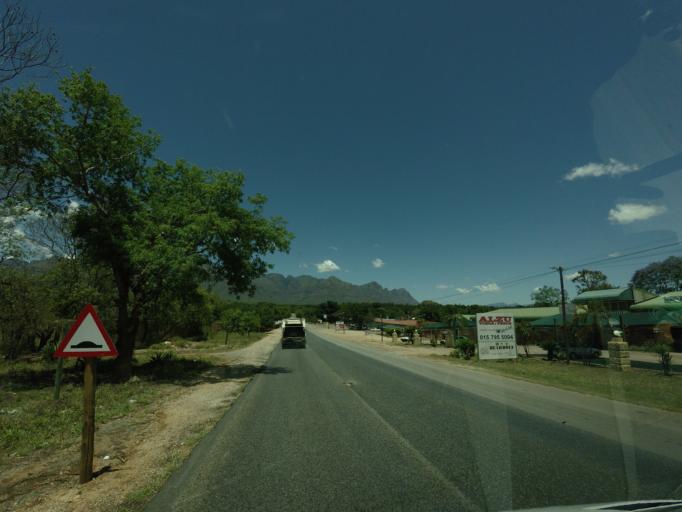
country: ZA
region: Limpopo
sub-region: Mopani District Municipality
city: Hoedspruit
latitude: -24.4033
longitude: 30.8008
